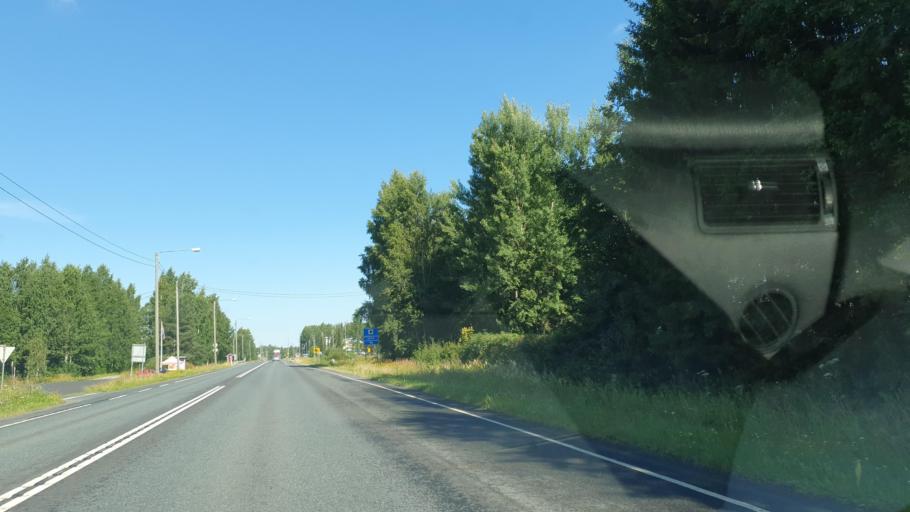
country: FI
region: Northern Savo
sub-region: Kuopio
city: Siilinjaervi
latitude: 63.1986
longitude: 27.5391
